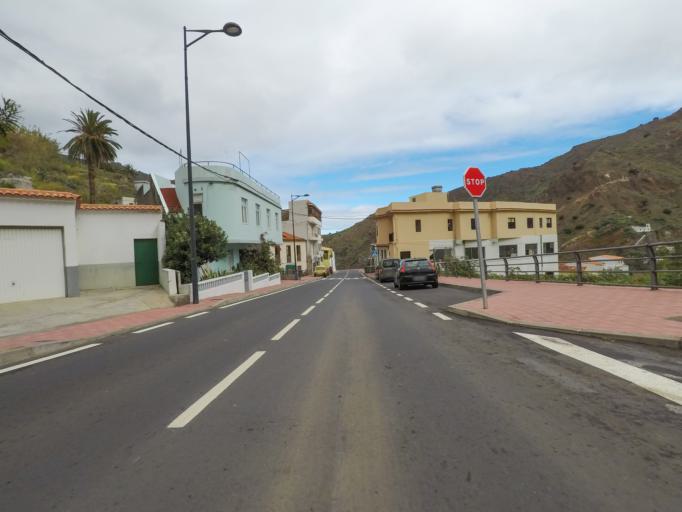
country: ES
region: Canary Islands
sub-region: Provincia de Santa Cruz de Tenerife
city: Hermigua
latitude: 28.1547
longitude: -17.1981
